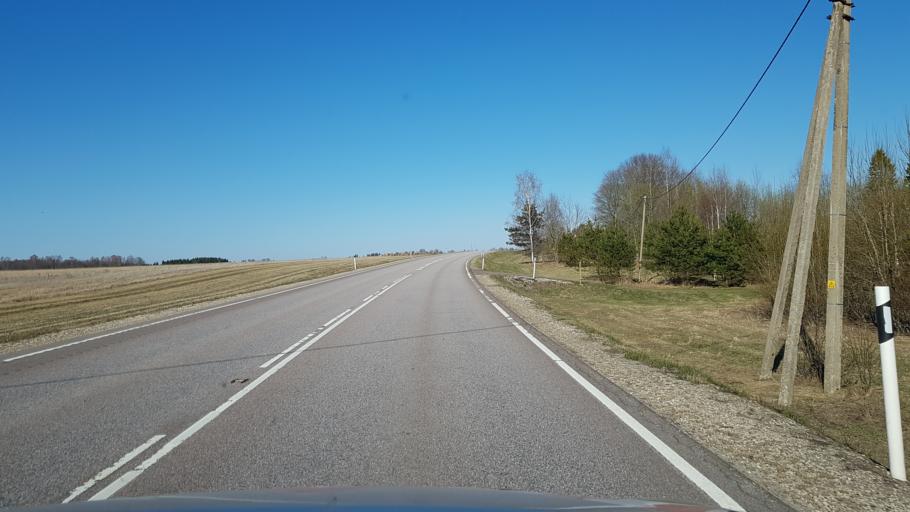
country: EE
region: Jogevamaa
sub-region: Mustvee linn
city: Mustvee
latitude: 58.7475
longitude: 26.8590
